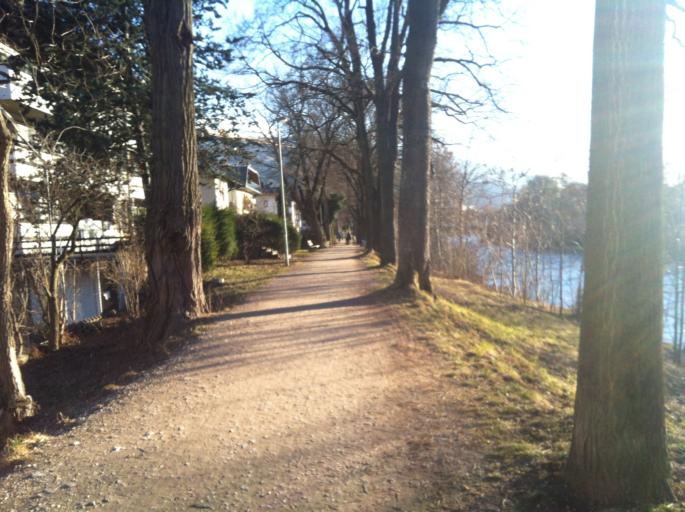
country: IT
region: Trentino-Alto Adige
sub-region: Bolzano
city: Bressanone
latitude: 46.7127
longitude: 11.6611
